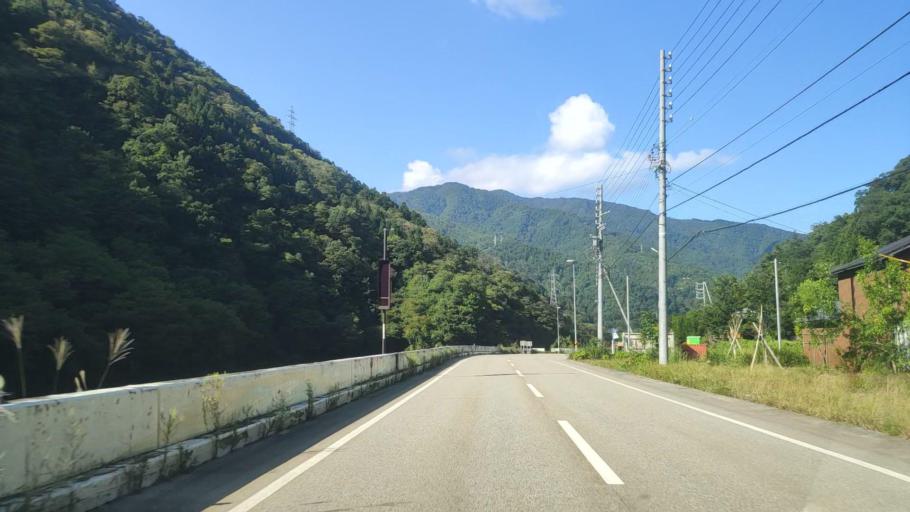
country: JP
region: Gifu
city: Takayama
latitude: 36.3186
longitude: 137.1336
